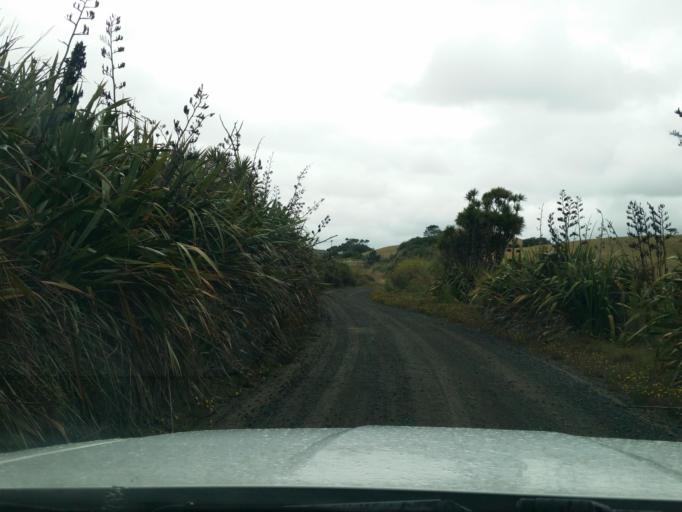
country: NZ
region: Northland
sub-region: Kaipara District
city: Dargaville
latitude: -35.9989
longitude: 173.7971
